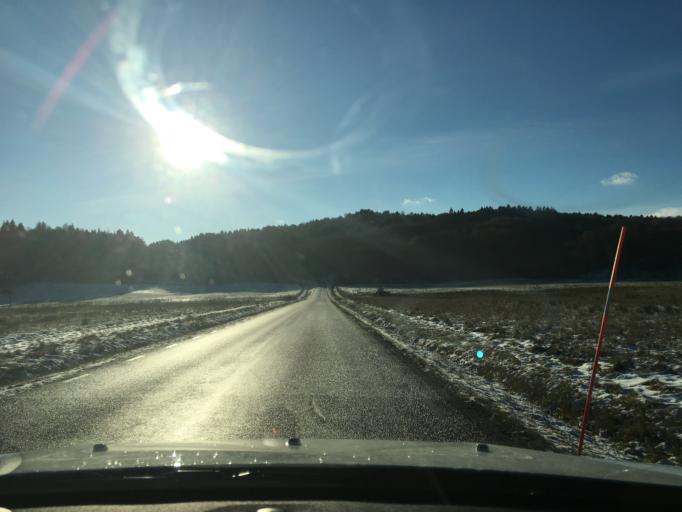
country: SE
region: Vaestra Goetaland
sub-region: Tjorns Kommun
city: Myggenas
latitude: 58.0536
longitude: 11.6752
